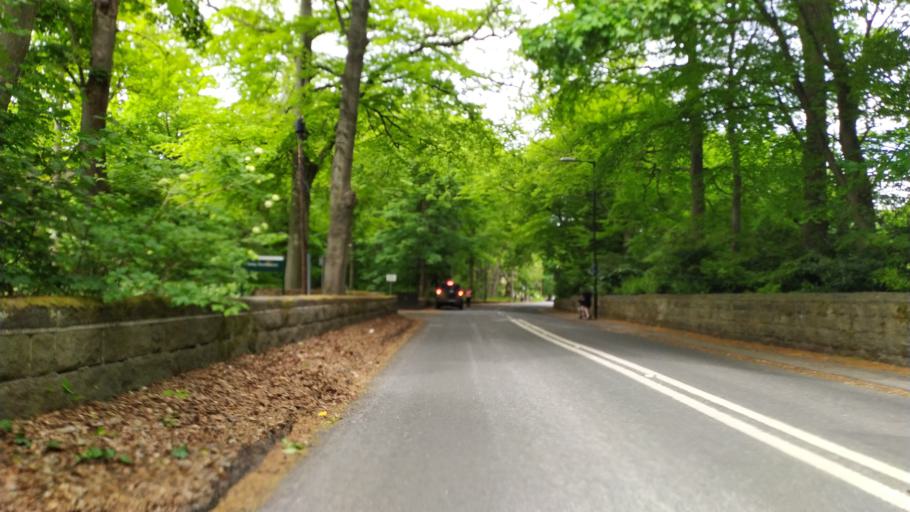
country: GB
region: England
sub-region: City and Borough of Leeds
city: Chapel Allerton
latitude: 53.8359
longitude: -1.5831
